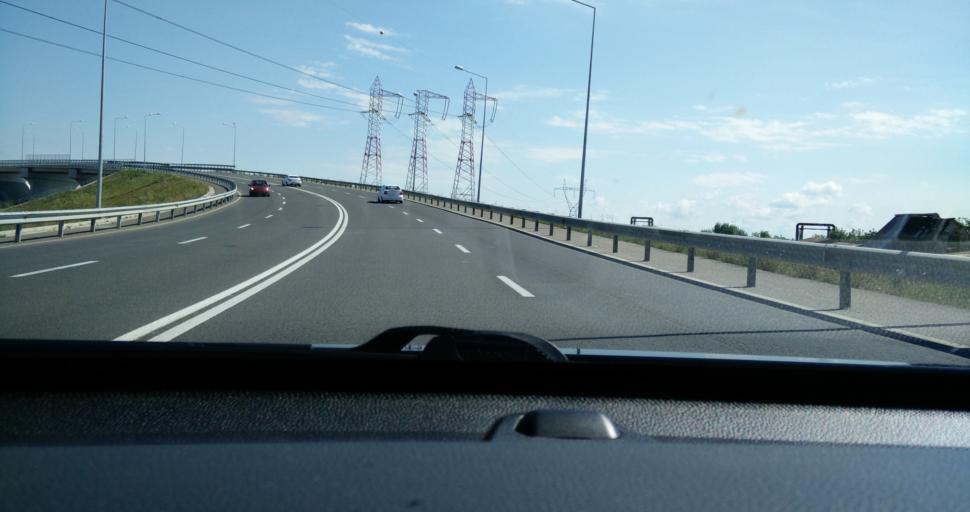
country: RO
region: Bihor
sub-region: Comuna Sanmartin
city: Sanmartin
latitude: 47.0323
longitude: 21.9938
